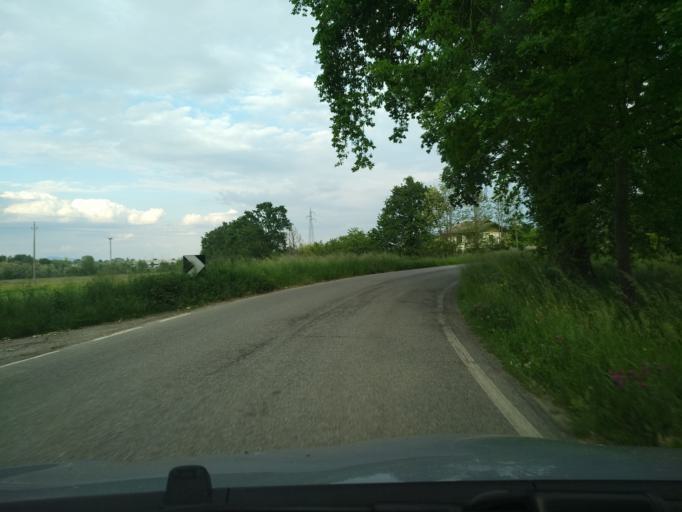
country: IT
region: Piedmont
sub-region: Provincia di Torino
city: Roletto
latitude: 44.9098
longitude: 7.3494
